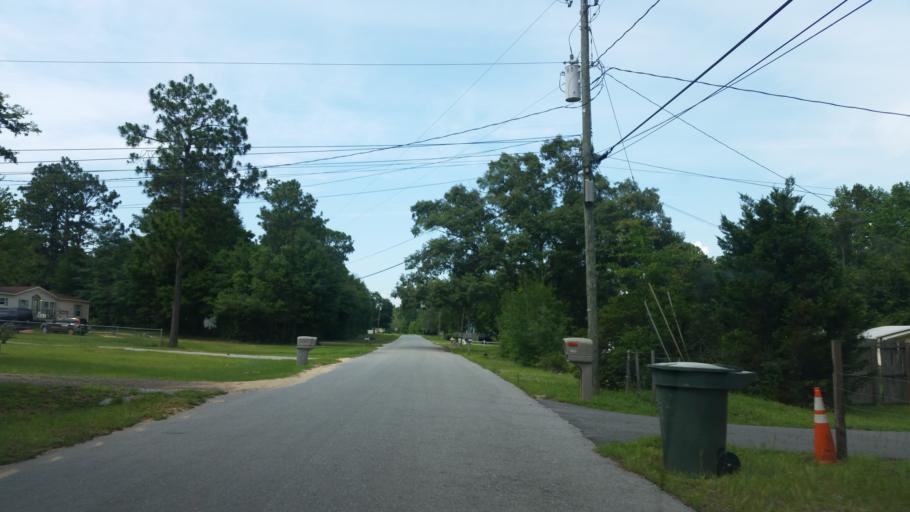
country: US
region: Florida
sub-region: Escambia County
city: Cantonment
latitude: 30.6395
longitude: -87.3873
